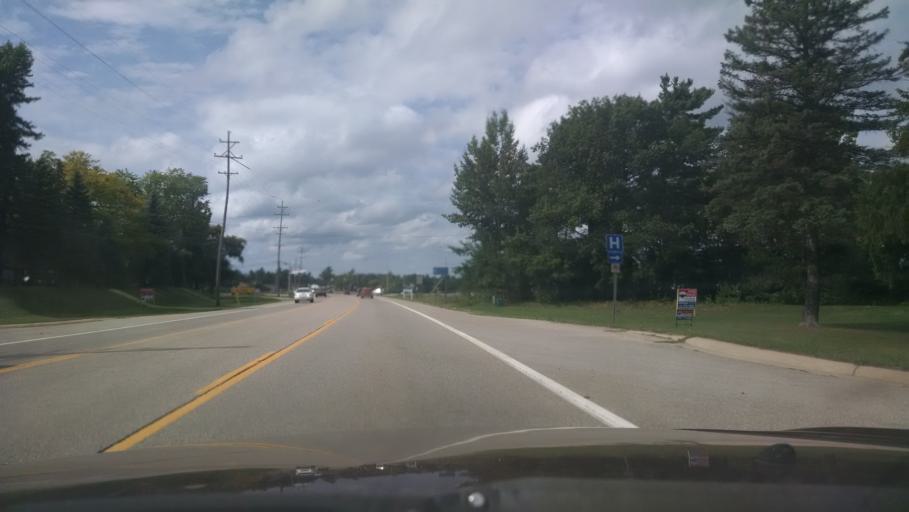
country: US
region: Michigan
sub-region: Wexford County
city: Cadillac
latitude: 44.2296
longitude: -85.4443
